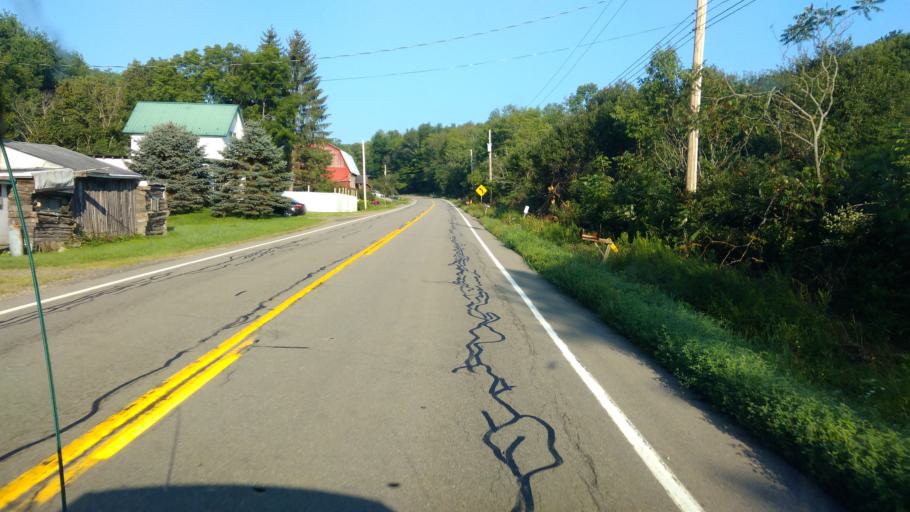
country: US
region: New York
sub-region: Allegany County
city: Andover
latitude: 42.1416
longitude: -77.6706
